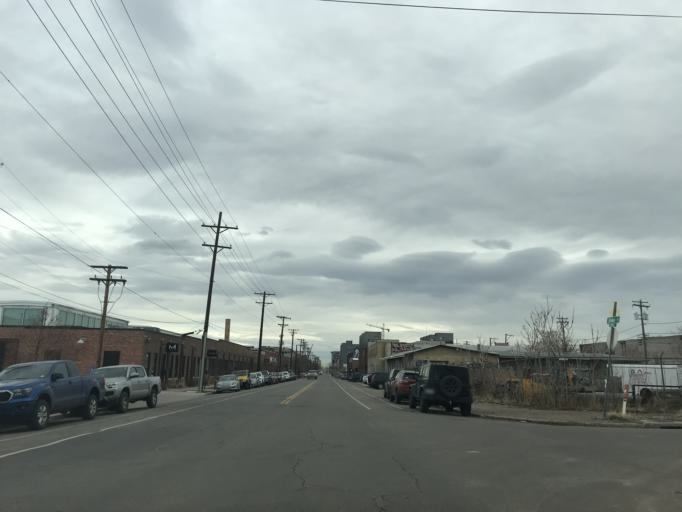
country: US
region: Colorado
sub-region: Denver County
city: Denver
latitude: 39.7626
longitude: -104.9836
